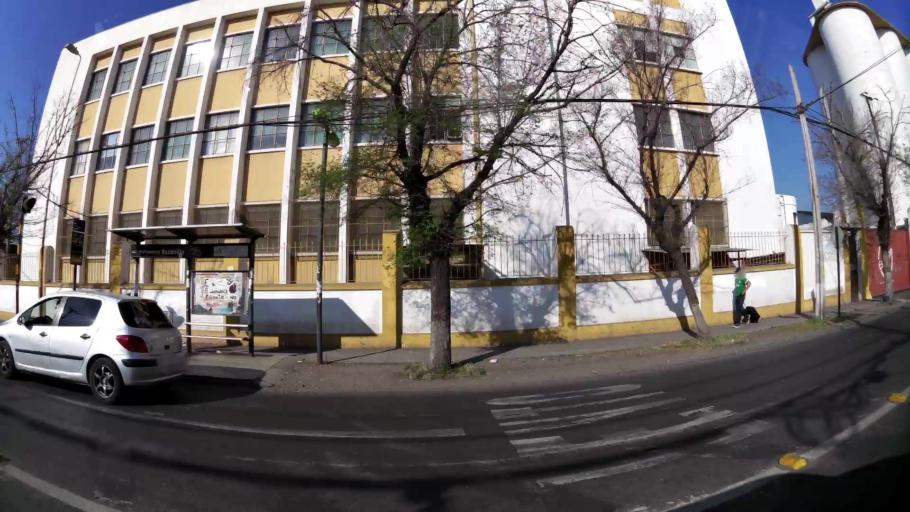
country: CL
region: Santiago Metropolitan
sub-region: Provincia de Santiago
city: Santiago
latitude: -33.4182
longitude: -70.6636
